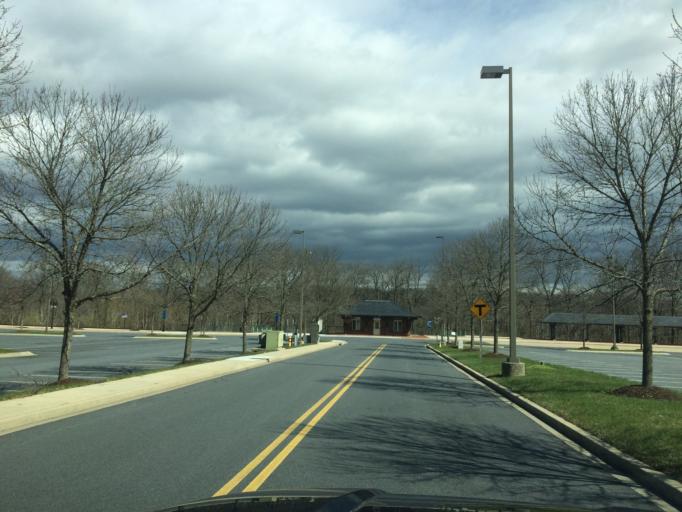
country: US
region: Maryland
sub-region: Frederick County
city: Frederick
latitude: 39.3822
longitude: -77.3958
